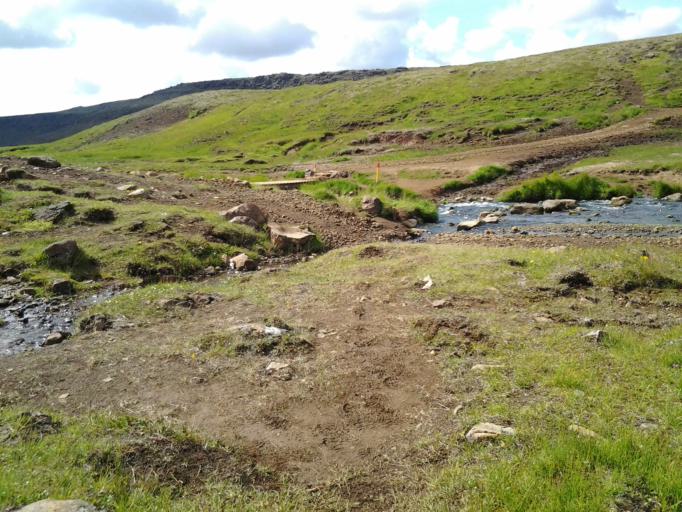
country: IS
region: South
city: Hveragerdi
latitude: 64.0404
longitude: -21.2187
